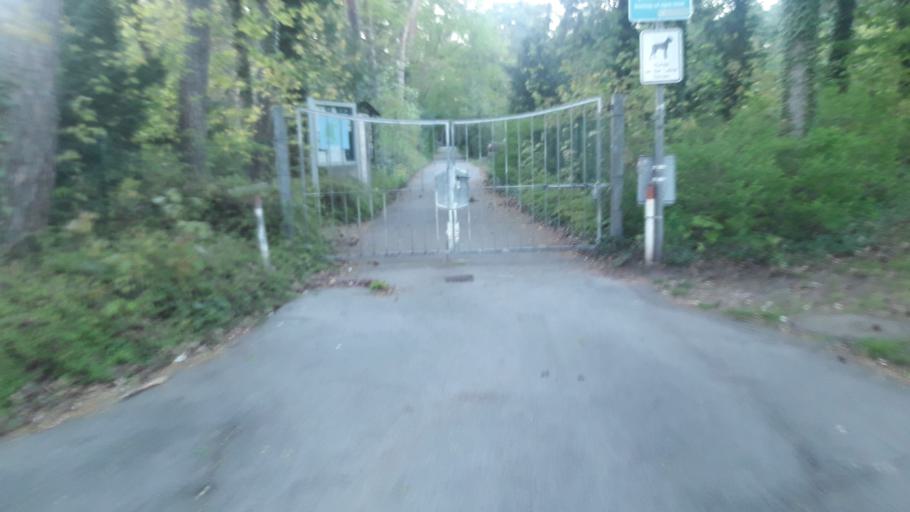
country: DE
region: North Rhine-Westphalia
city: Bad Lippspringe
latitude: 51.7826
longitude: 8.7998
